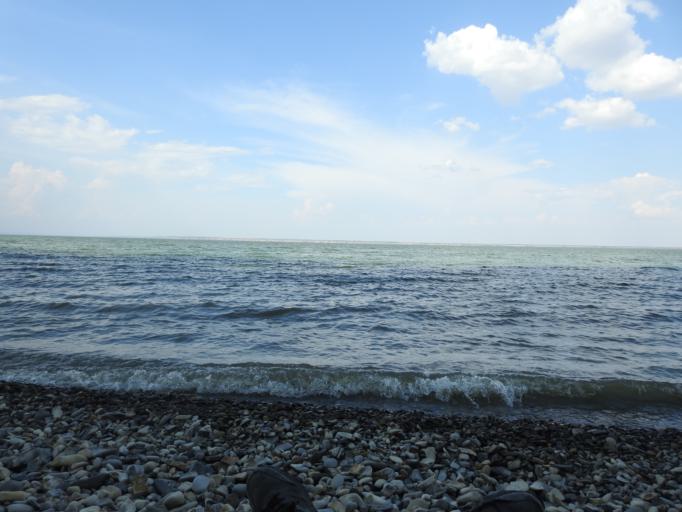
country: RU
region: Saratov
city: Rovnoye
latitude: 50.4977
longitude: 45.7942
